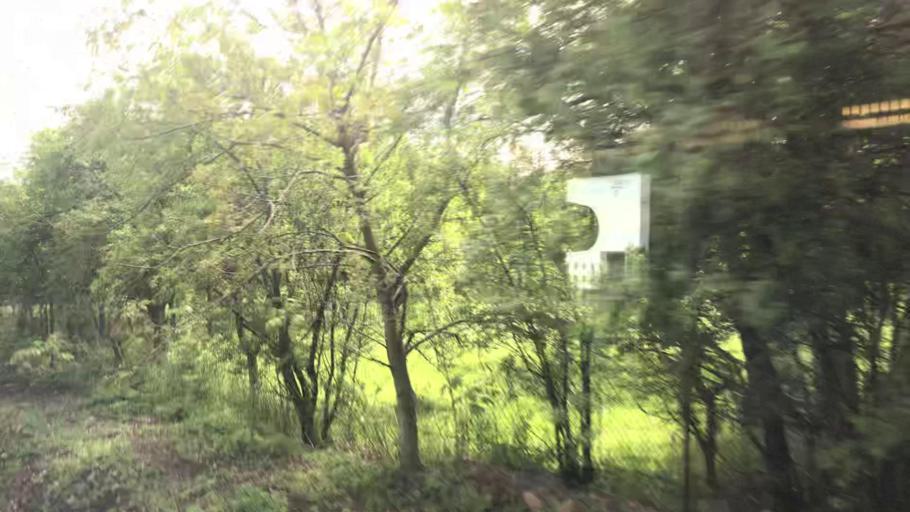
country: PL
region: Lower Silesian Voivodeship
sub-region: Powiat swidnicki
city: Swiebodzice
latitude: 50.8590
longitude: 16.3429
